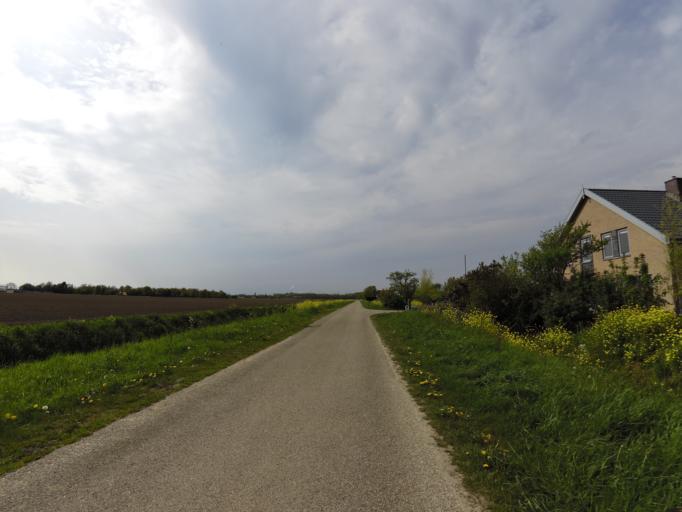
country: NL
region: South Holland
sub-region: Gemeente Brielle
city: Brielle
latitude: 51.9180
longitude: 4.1555
